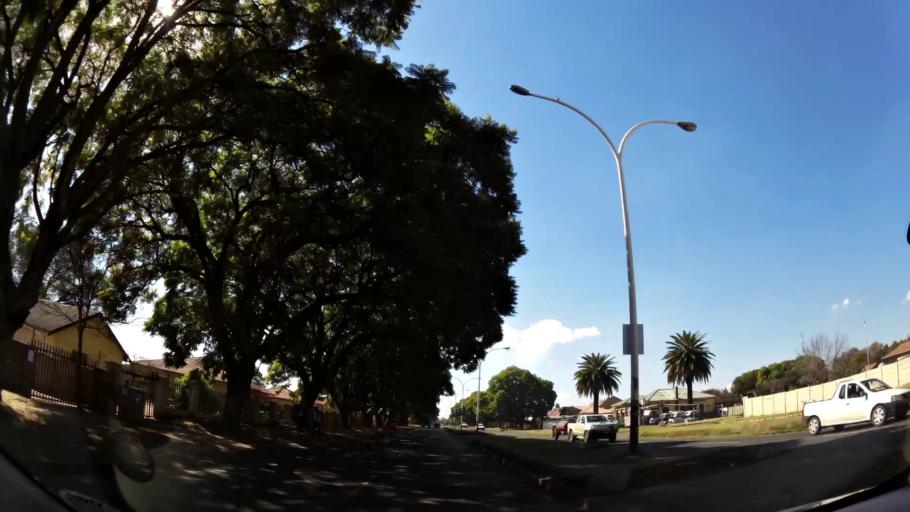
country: ZA
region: Mpumalanga
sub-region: Nkangala District Municipality
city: Witbank
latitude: -25.8679
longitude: 29.2160
